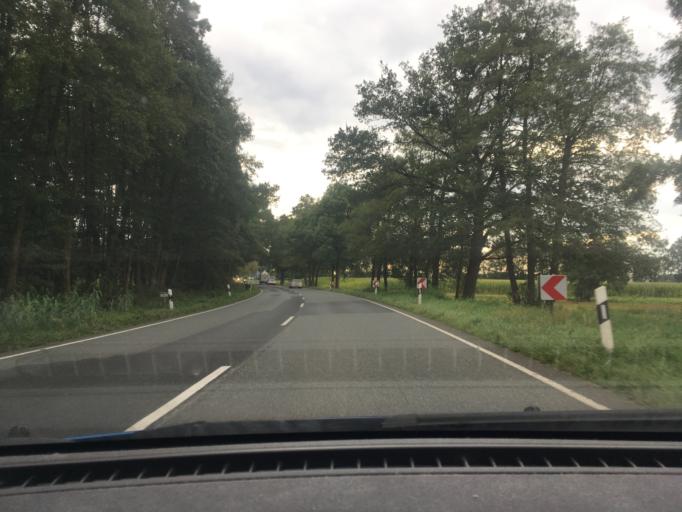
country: DE
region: Lower Saxony
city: Eschede
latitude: 52.7462
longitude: 10.2492
